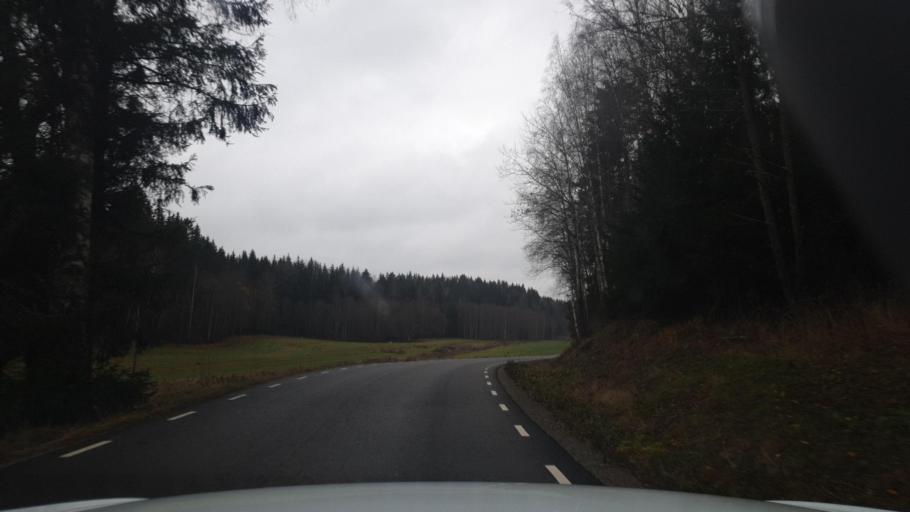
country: SE
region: Vaermland
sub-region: Arvika Kommun
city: Arvika
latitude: 59.6412
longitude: 12.8124
